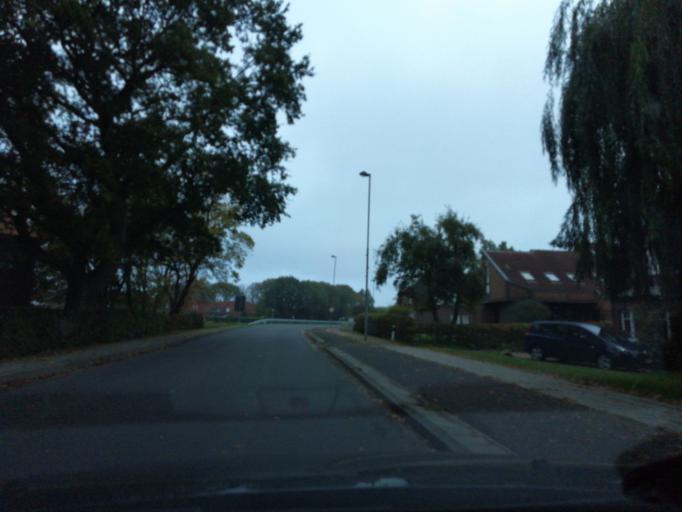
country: DE
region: Lower Saxony
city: Werdum
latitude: 53.6935
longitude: 7.8064
